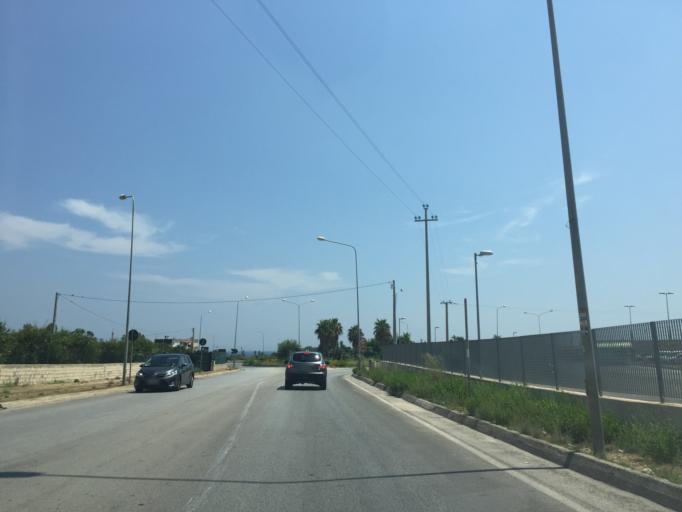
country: IT
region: Sicily
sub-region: Provincia di Siracusa
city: Avola
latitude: 36.9203
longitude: 15.1458
